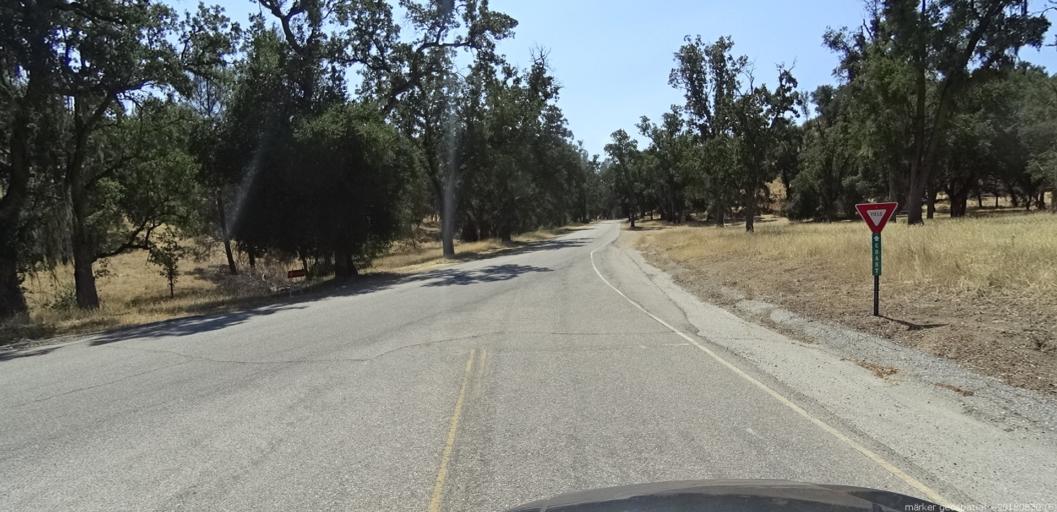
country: US
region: California
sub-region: Monterey County
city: King City
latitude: 35.9799
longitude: -121.2583
